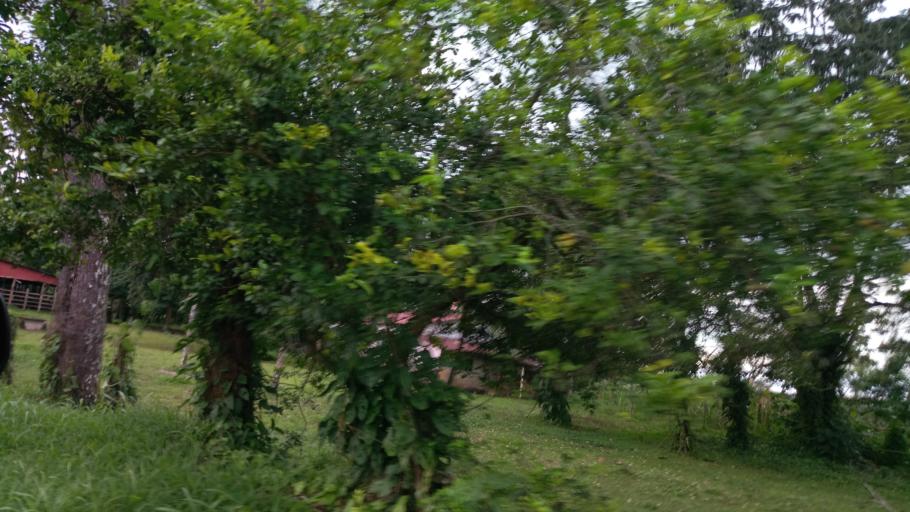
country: CR
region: Alajuela
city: Pocosol
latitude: 10.3740
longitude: -84.5638
